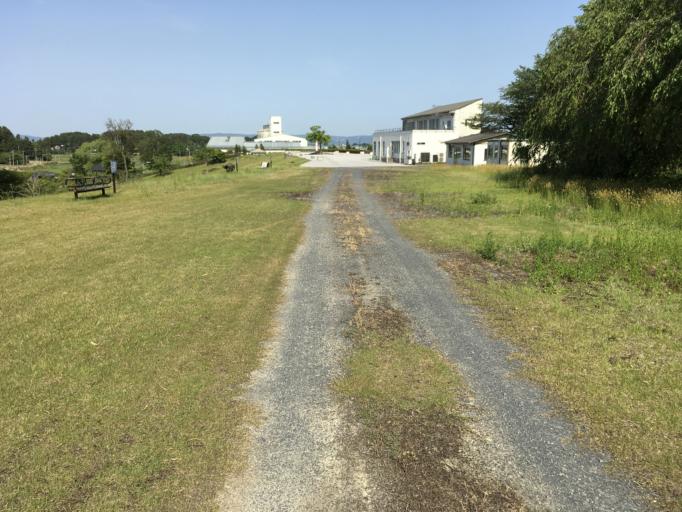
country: JP
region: Miyagi
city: Wakuya
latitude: 38.6681
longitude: 141.1396
